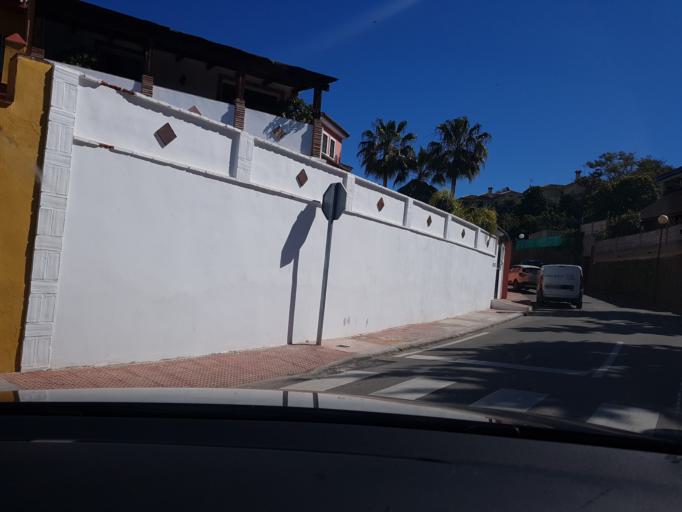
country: ES
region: Andalusia
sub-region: Provincia de Malaga
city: Marbella
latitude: 36.5204
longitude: -4.8886
